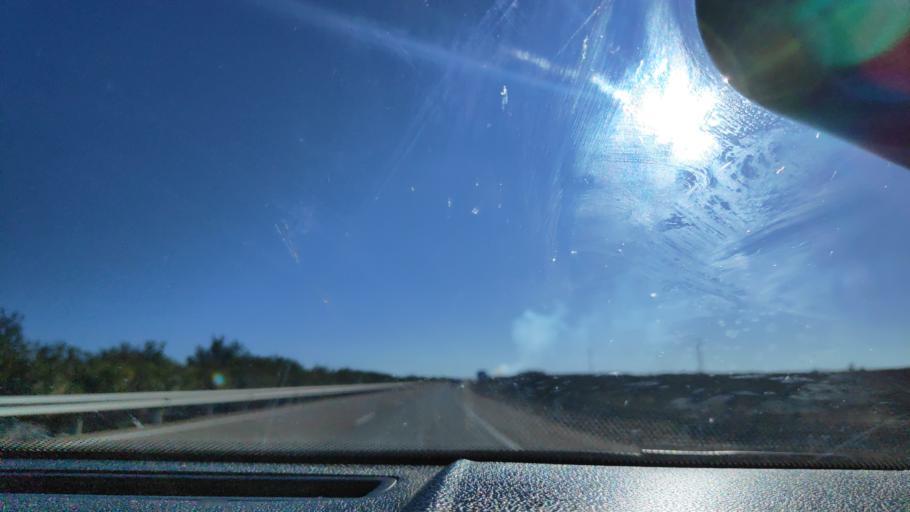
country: ES
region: Extremadura
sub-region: Provincia de Badajoz
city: Los Santos de Maimona
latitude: 38.4889
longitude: -6.3555
